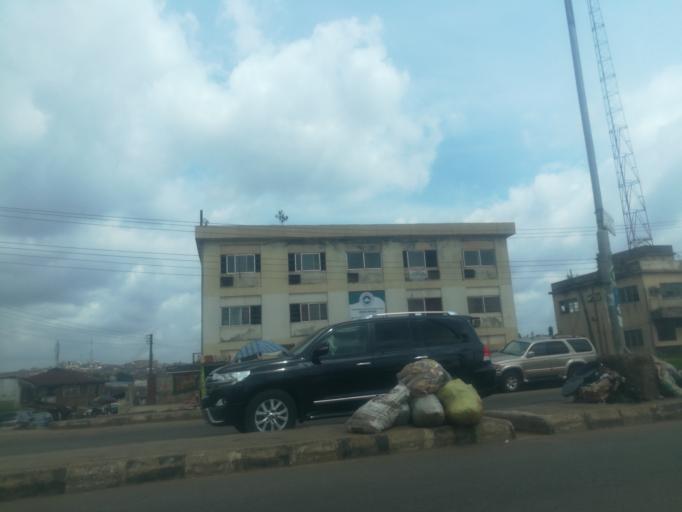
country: NG
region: Oyo
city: Ibadan
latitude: 7.3648
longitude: 3.8852
